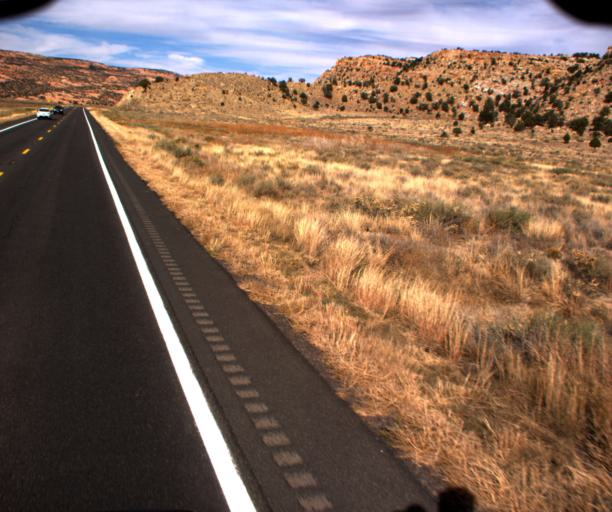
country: US
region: Arizona
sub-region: Navajo County
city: Kayenta
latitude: 36.6038
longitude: -110.4728
